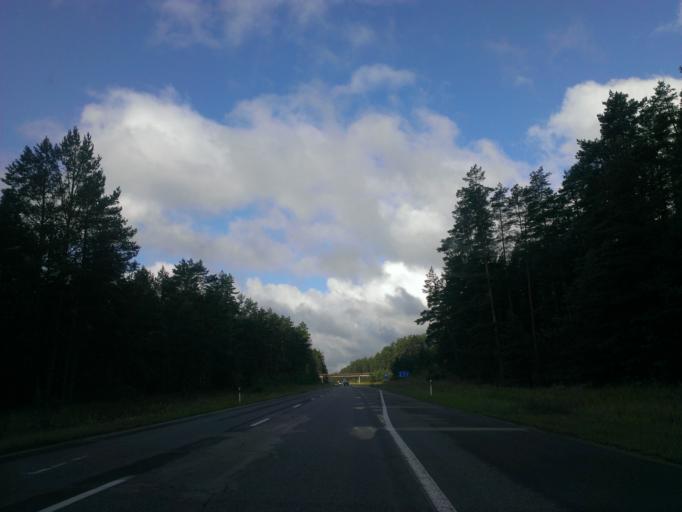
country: LV
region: Incukalns
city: Vangazi
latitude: 57.0824
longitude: 24.5270
